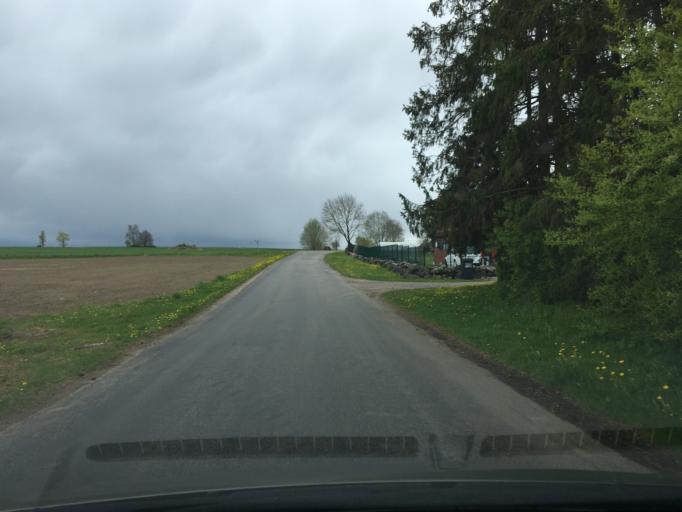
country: EE
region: Harju
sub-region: Rae vald
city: Vaida
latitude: 59.3633
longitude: 24.9701
